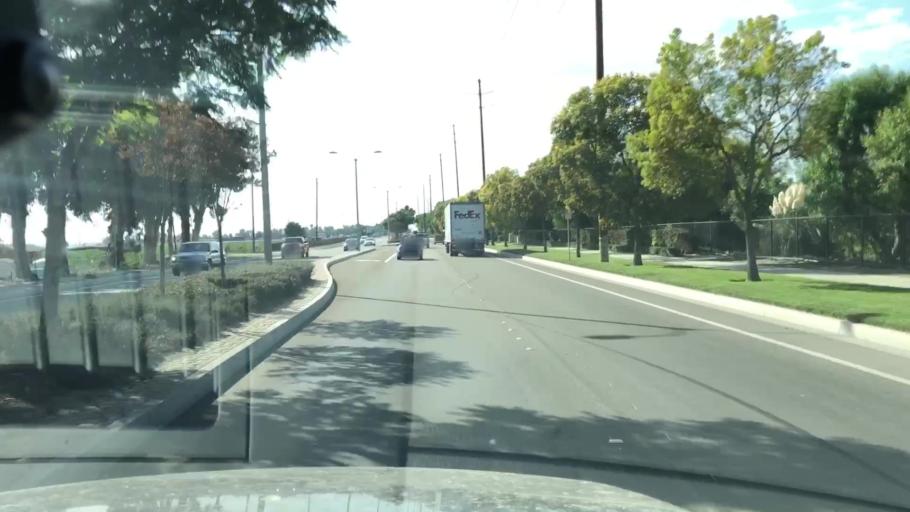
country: US
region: California
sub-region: Ventura County
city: Camarillo
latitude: 34.2055
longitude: -119.0281
